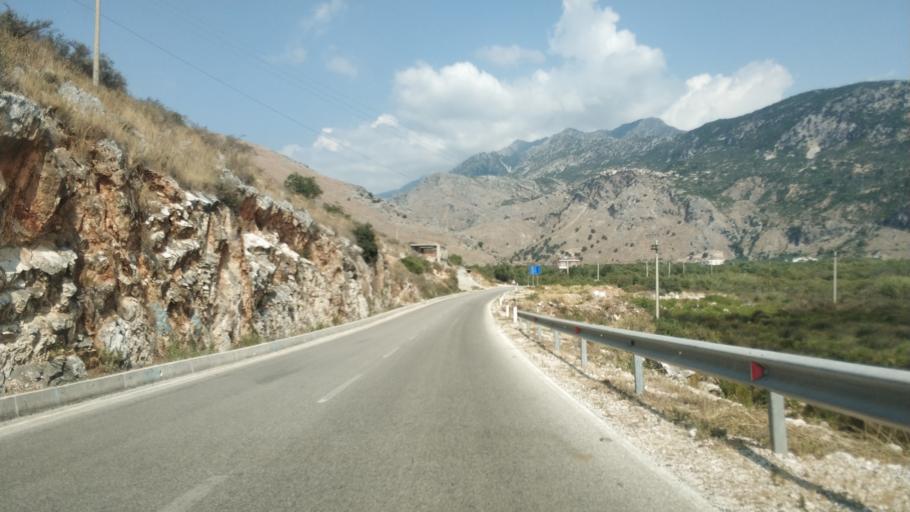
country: AL
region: Vlore
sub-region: Rrethi i Vlores
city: Himare
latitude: 40.0522
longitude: 19.8127
